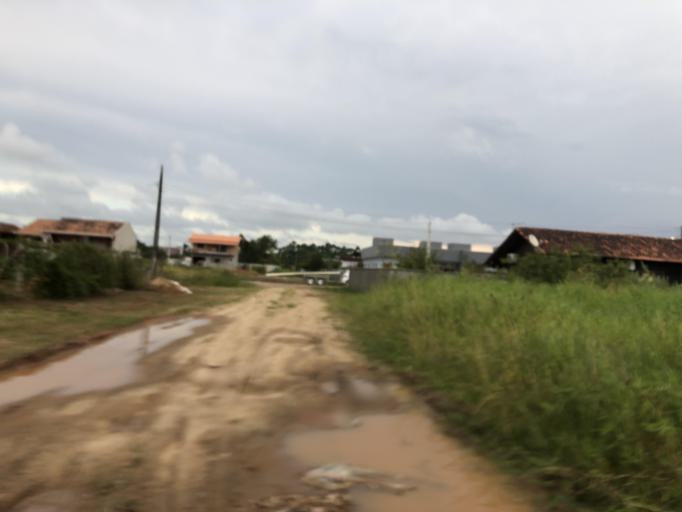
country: BR
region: Santa Catarina
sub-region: Sao Francisco Do Sul
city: Sao Francisco do Sul
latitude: -26.2180
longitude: -48.5342
